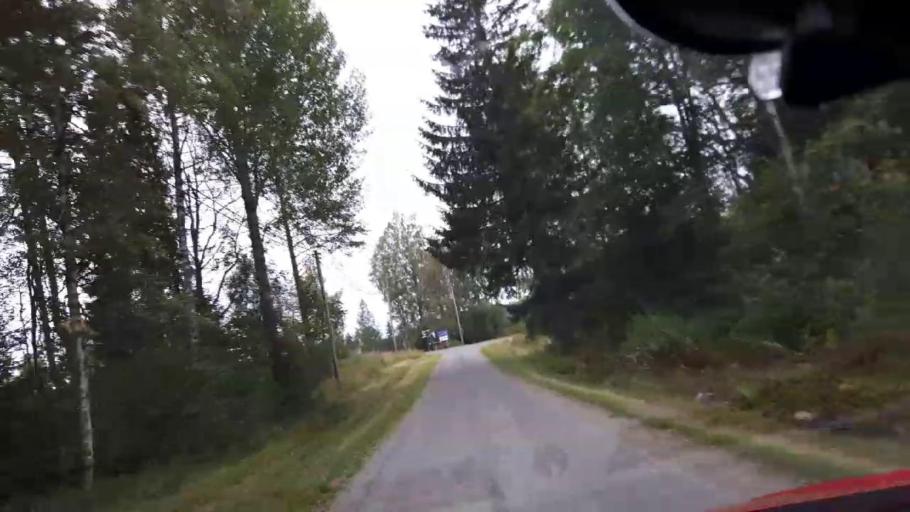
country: SE
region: Vaesternorrland
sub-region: Ange Kommun
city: Ange
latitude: 62.8533
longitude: 15.9058
